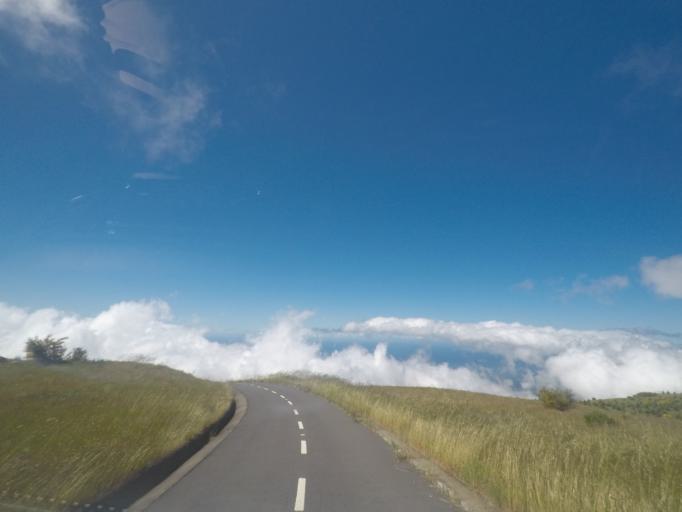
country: PT
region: Madeira
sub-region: Camara de Lobos
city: Curral das Freiras
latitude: 32.7130
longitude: -16.9385
